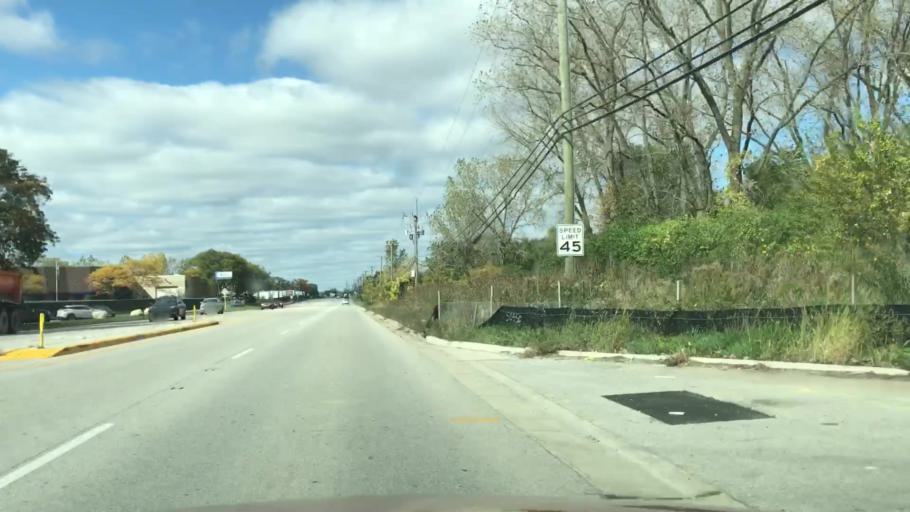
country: US
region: Illinois
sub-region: Cook County
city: Elk Grove Village
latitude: 42.0157
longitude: -87.9504
